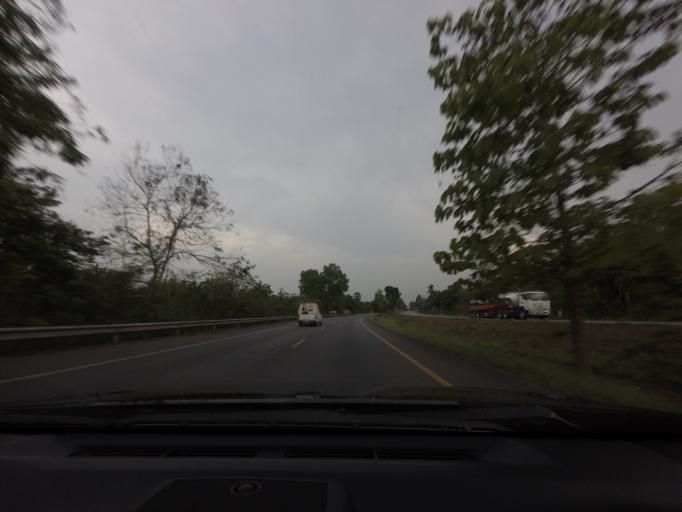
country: TH
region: Surat Thani
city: Chaiya
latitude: 9.4633
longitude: 99.1536
